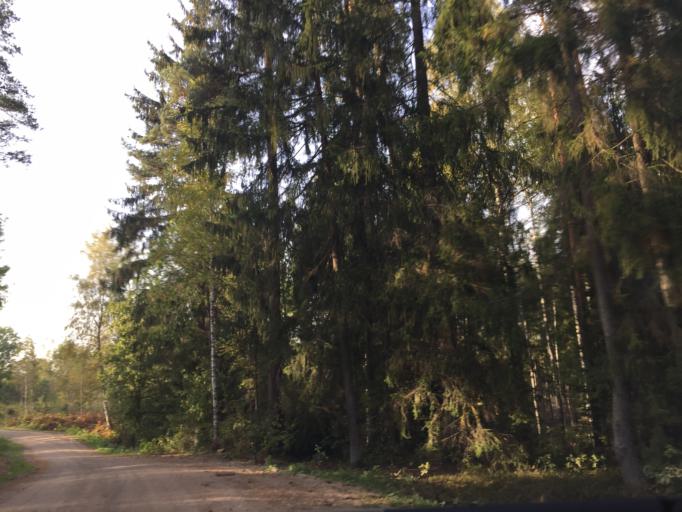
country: LV
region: Garkalne
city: Garkalne
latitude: 56.9726
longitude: 24.4224
